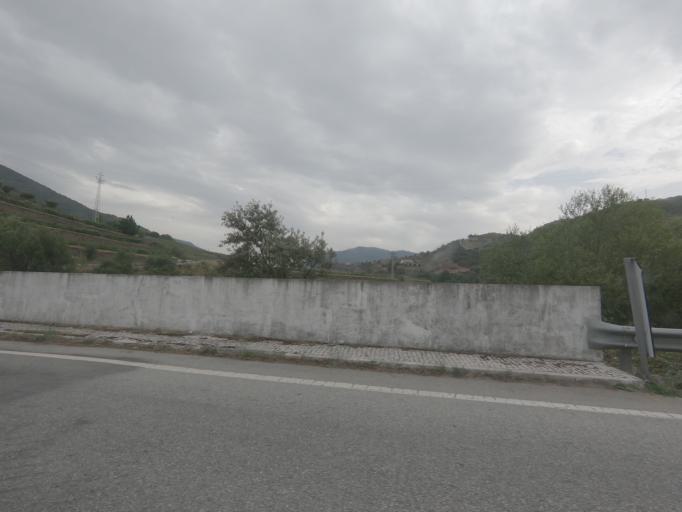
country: PT
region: Viseu
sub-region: Armamar
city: Armamar
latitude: 41.1575
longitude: -7.6419
